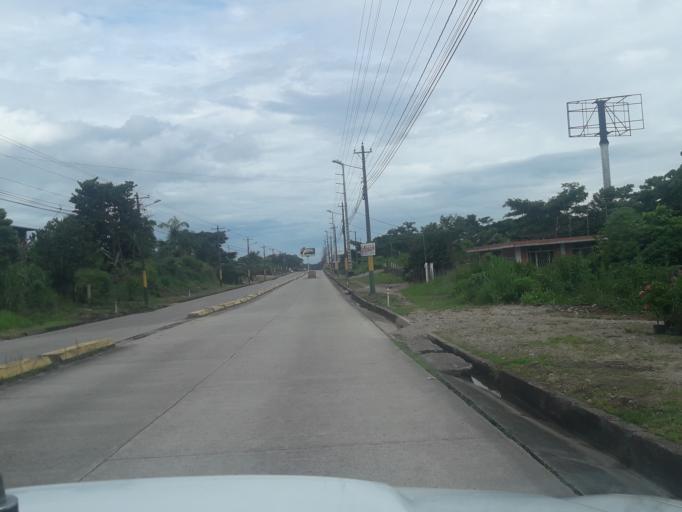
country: EC
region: Napo
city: Tena
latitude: -0.9519
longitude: -77.8167
